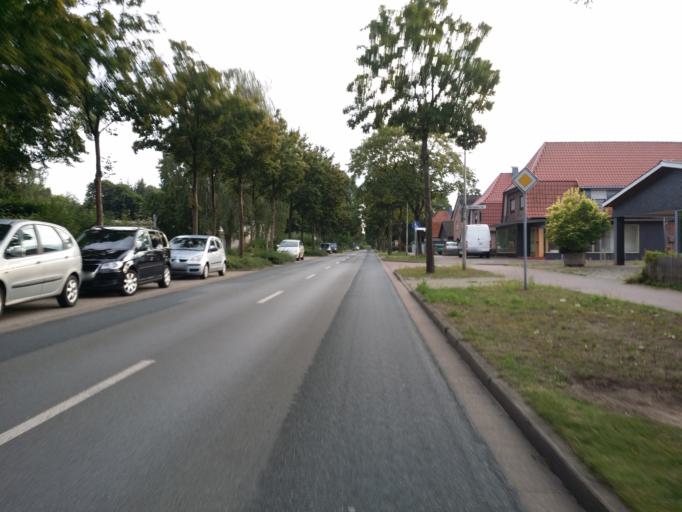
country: DE
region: Lower Saxony
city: Bremervorde
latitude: 53.4774
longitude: 9.1380
